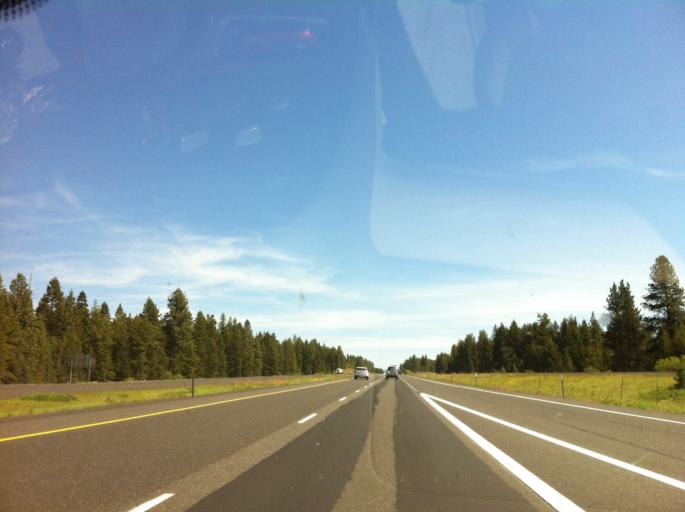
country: US
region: Oregon
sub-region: Umatilla County
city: Mission
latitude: 45.5053
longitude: -118.4252
